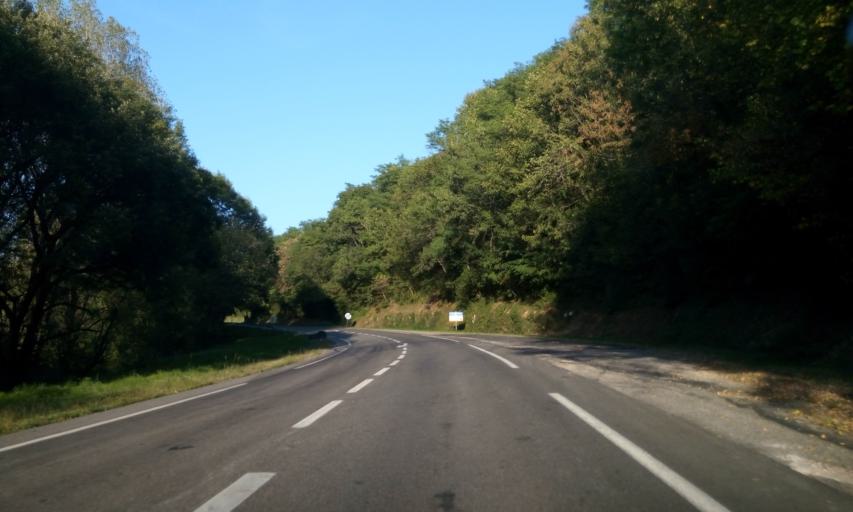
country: FR
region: Rhone-Alpes
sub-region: Departement de l'Ain
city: Poncin
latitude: 46.0746
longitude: 5.4532
